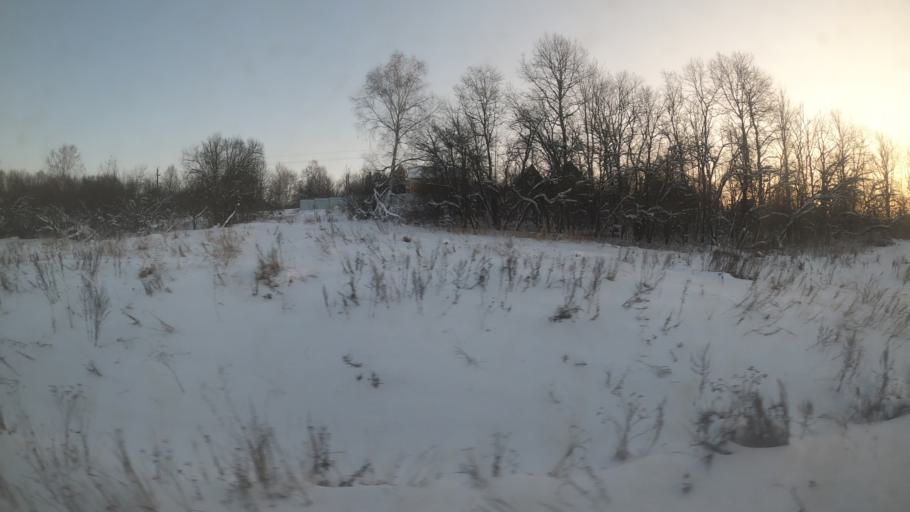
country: RU
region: Moskovskaya
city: Dedenevo
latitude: 56.2737
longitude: 37.5077
